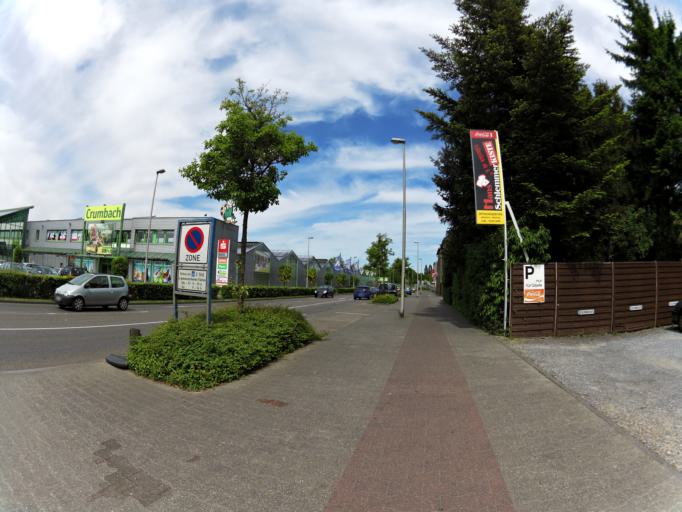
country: NL
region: Limburg
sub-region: Gemeente Kerkrade
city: Kerkrade
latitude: 50.8336
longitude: 6.0773
